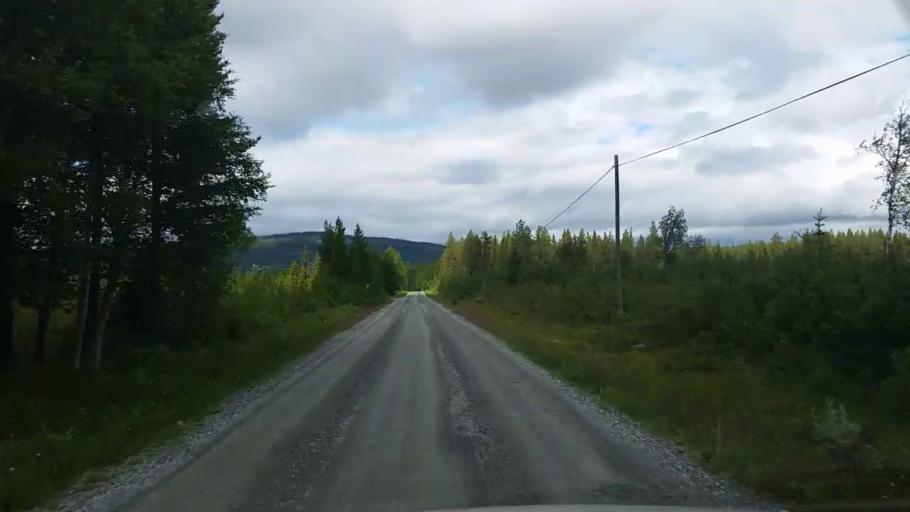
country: NO
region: Hedmark
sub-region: Engerdal
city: Engerdal
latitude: 62.4145
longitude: 12.6771
